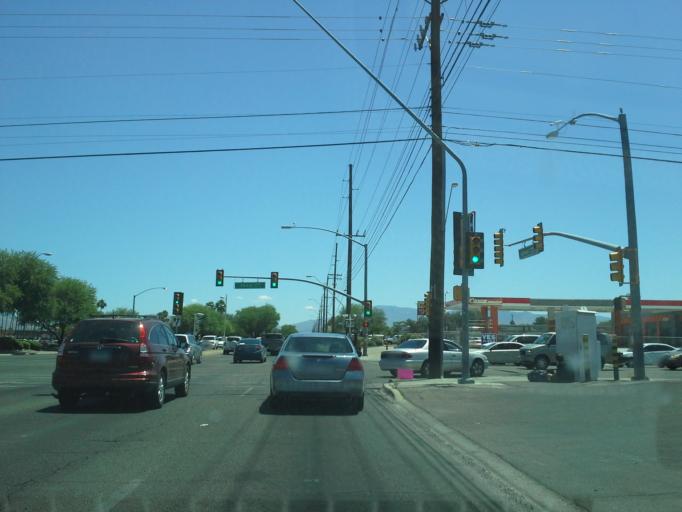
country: US
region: Arizona
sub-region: Pima County
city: Tucson
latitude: 32.2506
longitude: -110.8931
